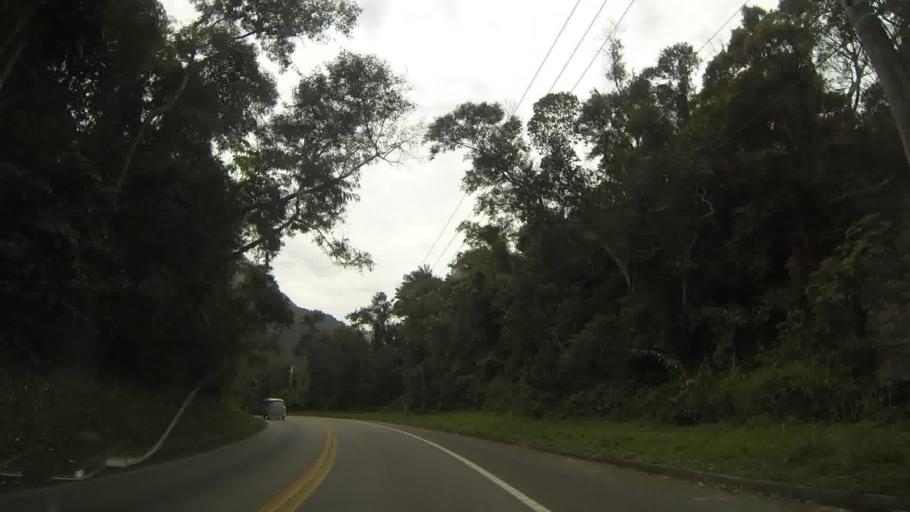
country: BR
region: Sao Paulo
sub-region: Sao Sebastiao
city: Sao Sebastiao
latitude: -23.8165
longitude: -45.4708
